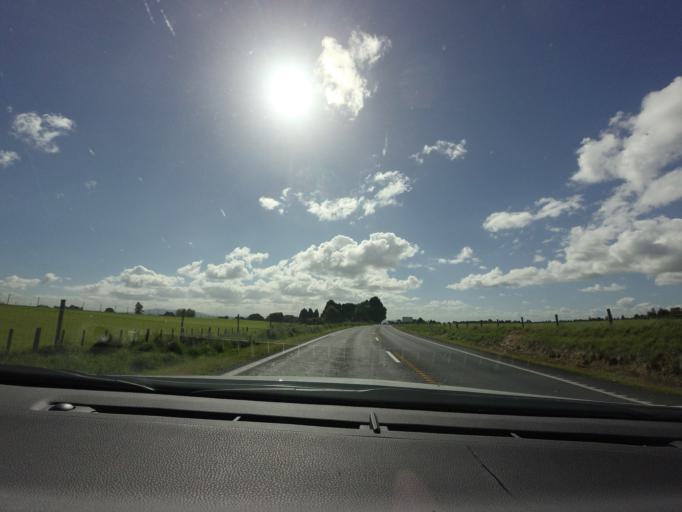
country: NZ
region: Waikato
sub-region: South Waikato District
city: Tokoroa
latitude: -38.0043
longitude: 175.9152
